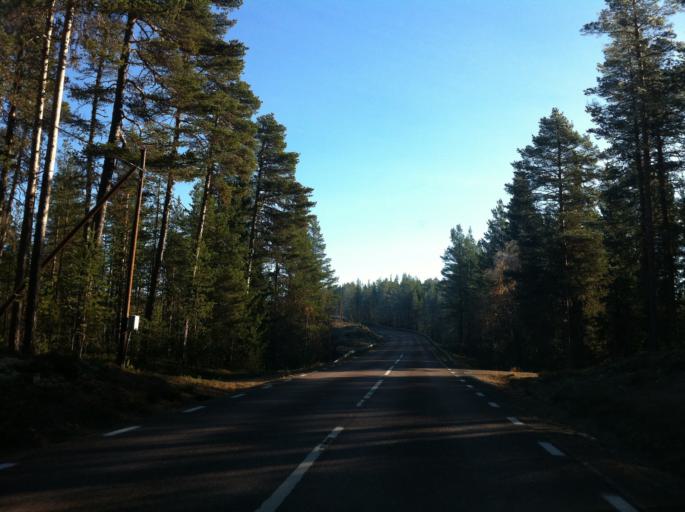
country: NO
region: Hedmark
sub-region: Trysil
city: Innbygda
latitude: 61.8456
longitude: 12.7771
